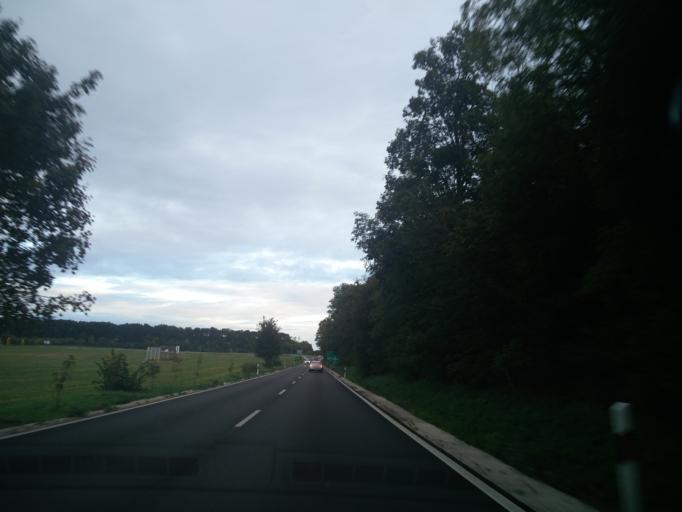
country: HU
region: Somogy
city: Balatonbereny
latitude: 46.6830
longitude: 17.3347
